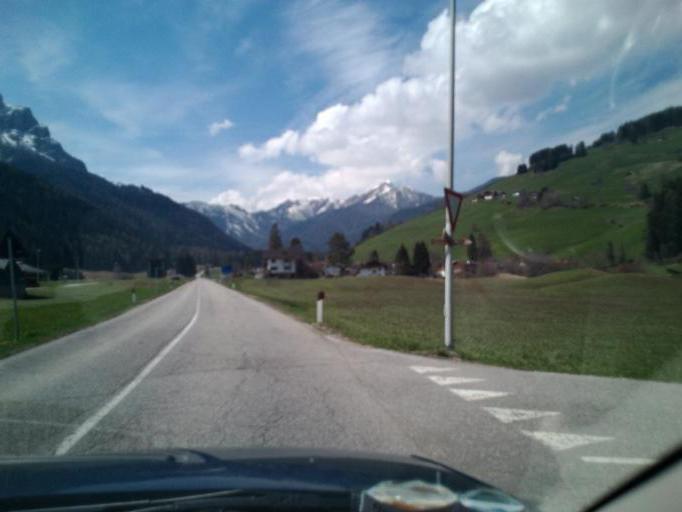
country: IT
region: Trentino-Alto Adige
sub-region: Bolzano
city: Braies
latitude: 46.7209
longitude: 12.1383
